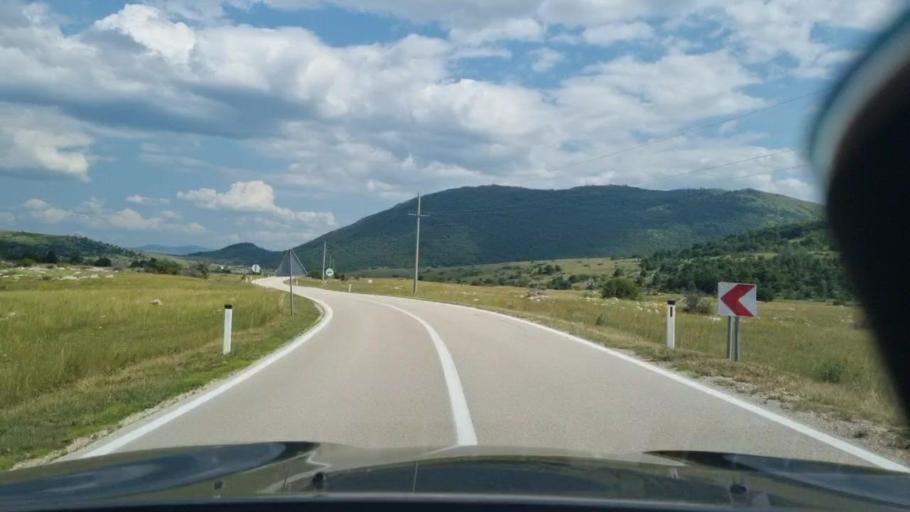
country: BA
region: Federation of Bosnia and Herzegovina
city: Bosansko Grahovo
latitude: 44.1436
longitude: 16.4637
